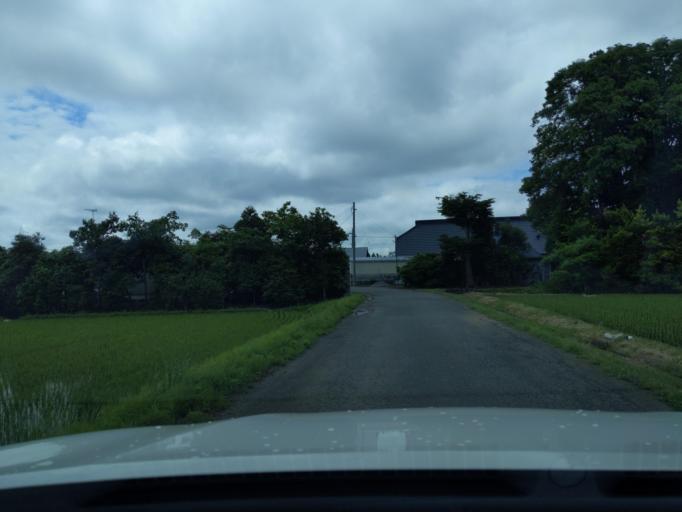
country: JP
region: Fukushima
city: Koriyama
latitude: 37.4195
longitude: 140.3262
